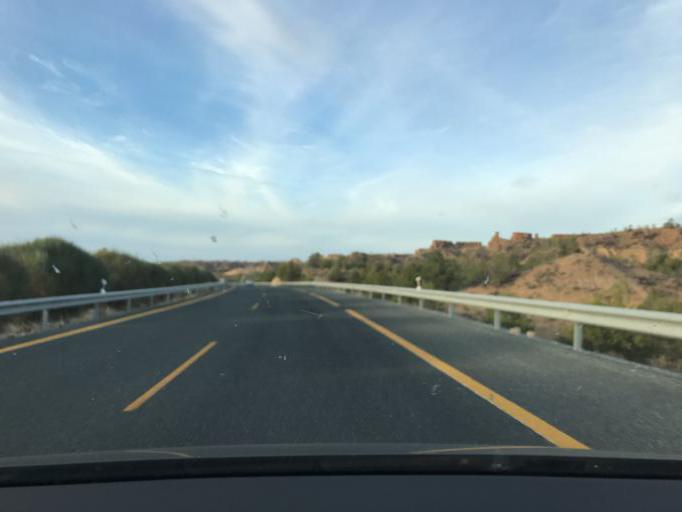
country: ES
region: Andalusia
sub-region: Provincia de Granada
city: Guadix
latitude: 37.3000
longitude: -3.1096
